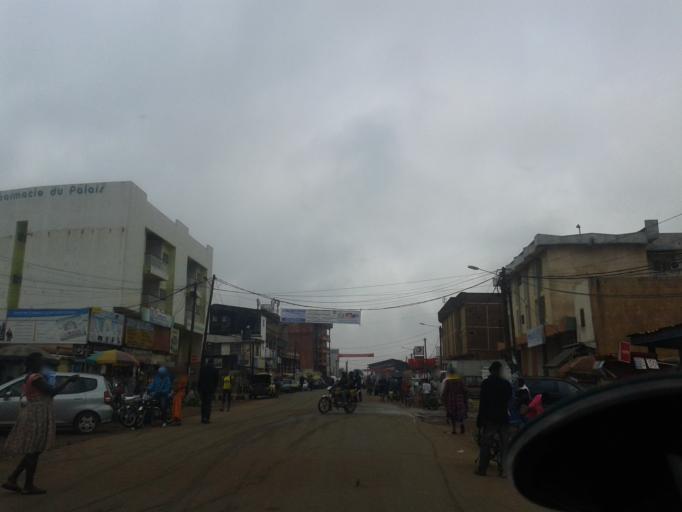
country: CM
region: Centre
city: Yaounde
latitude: 3.9133
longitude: 11.5262
